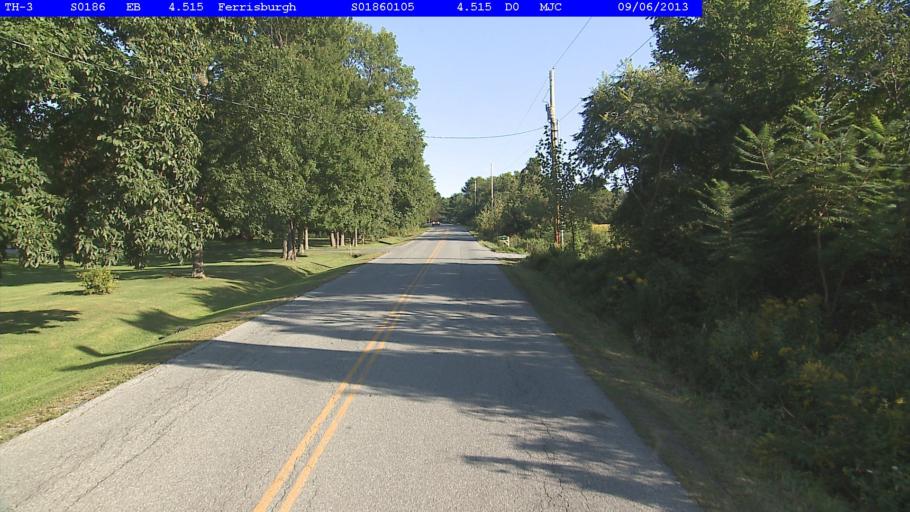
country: US
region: Vermont
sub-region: Addison County
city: Vergennes
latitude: 44.1646
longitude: -73.2953
